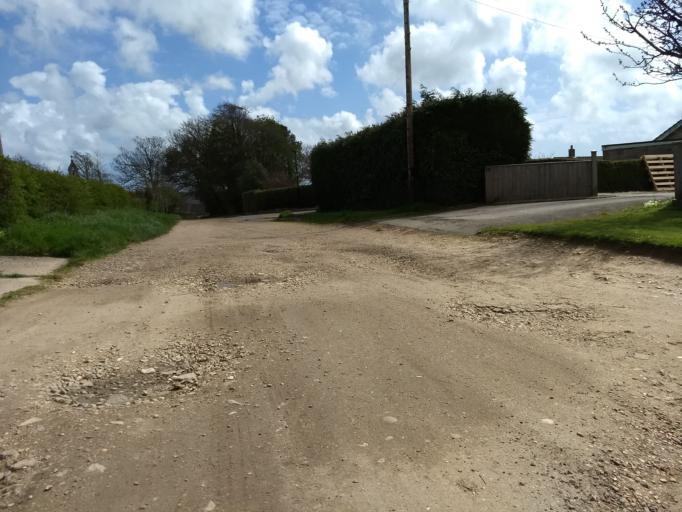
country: GB
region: England
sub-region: Isle of Wight
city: East Cowes
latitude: 50.7311
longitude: -1.2358
